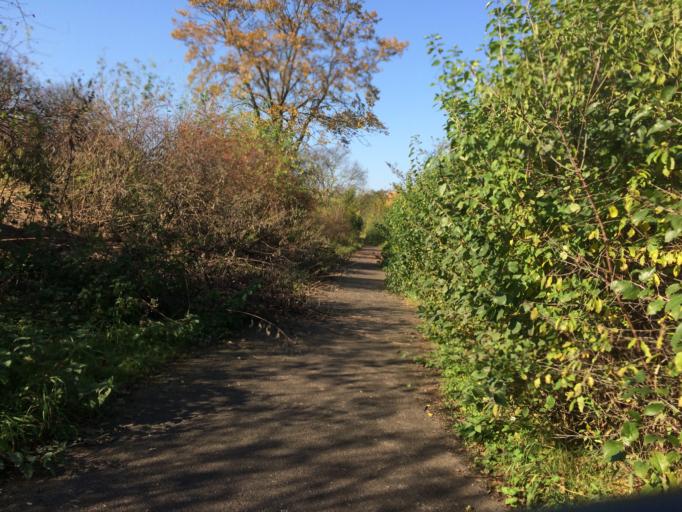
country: DE
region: Berlin
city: Buchholz
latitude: 52.6316
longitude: 13.4240
